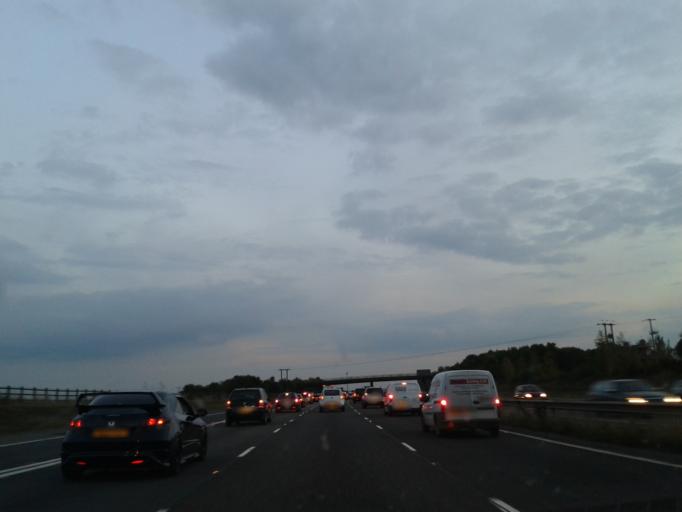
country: GB
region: England
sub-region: Oxfordshire
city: Bicester
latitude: 51.9428
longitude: -1.2026
